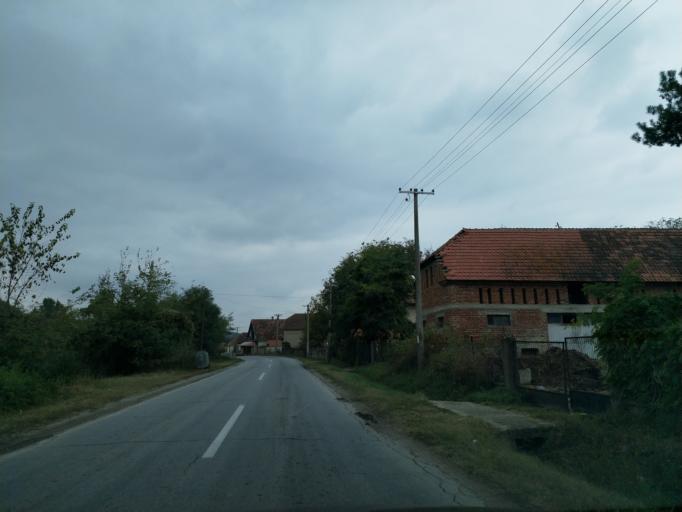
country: RS
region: Central Serbia
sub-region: Pomoravski Okrug
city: Jagodina
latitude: 44.0630
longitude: 21.1819
